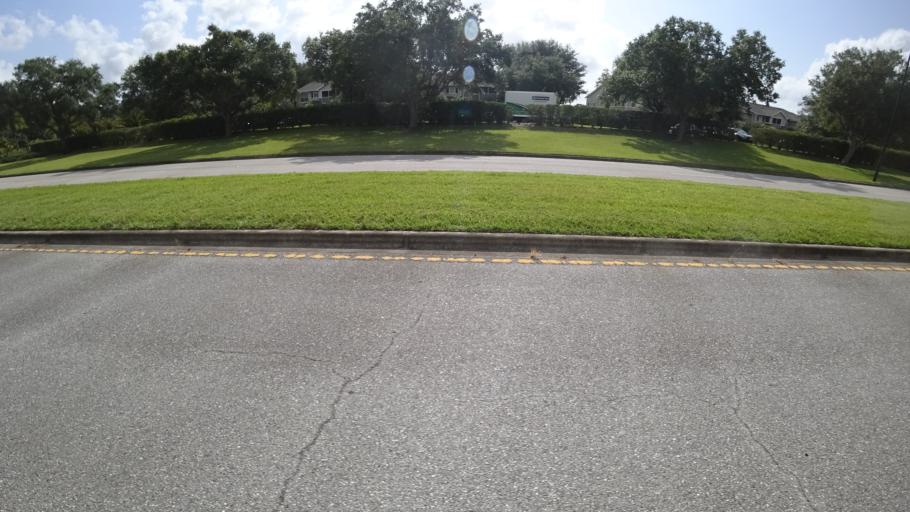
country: US
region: Florida
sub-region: Sarasota County
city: The Meadows
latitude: 27.4046
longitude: -82.4505
